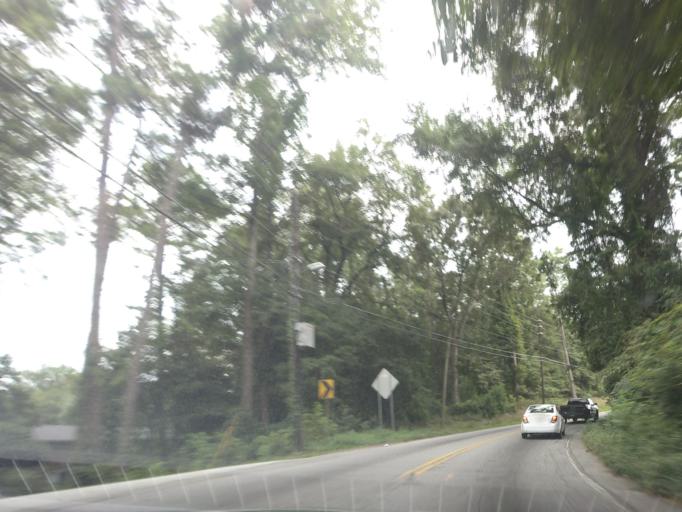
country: US
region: Georgia
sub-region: Bibb County
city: Macon
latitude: 32.8693
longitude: -83.6896
